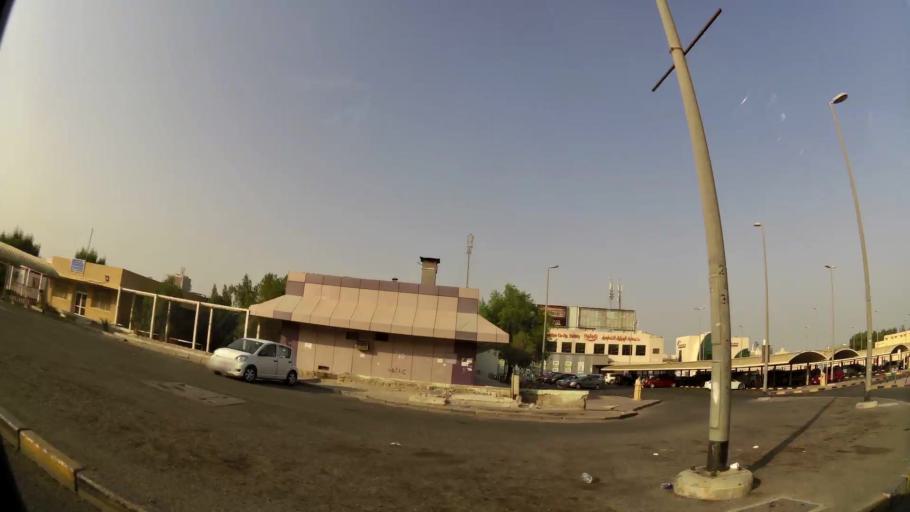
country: KW
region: Muhafazat Hawalli
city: Ar Rumaythiyah
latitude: 29.3160
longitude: 48.0781
